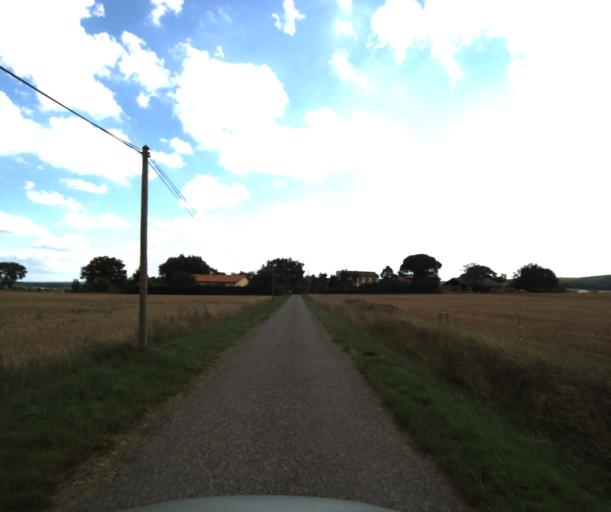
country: FR
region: Midi-Pyrenees
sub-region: Departement de la Haute-Garonne
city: Eaunes
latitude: 43.4214
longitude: 1.3631
